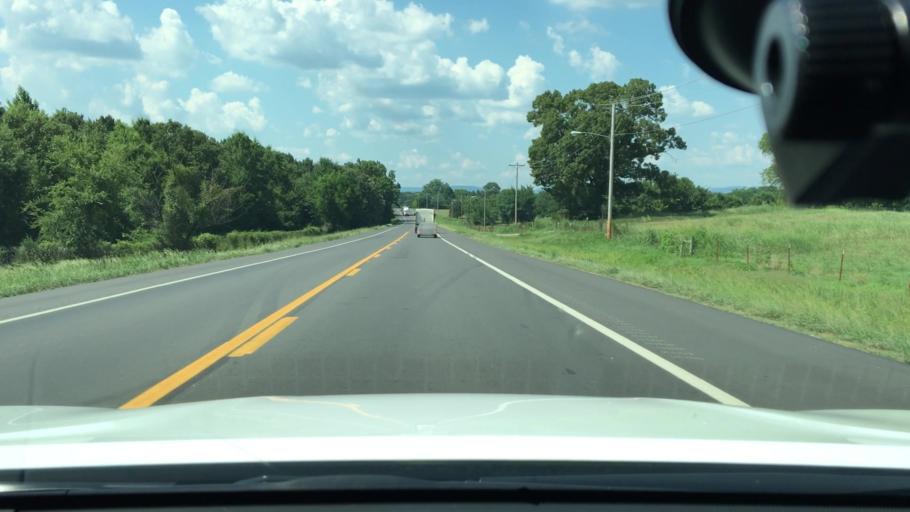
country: US
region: Arkansas
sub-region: Johnson County
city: Clarksville
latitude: 35.4418
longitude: -93.5292
